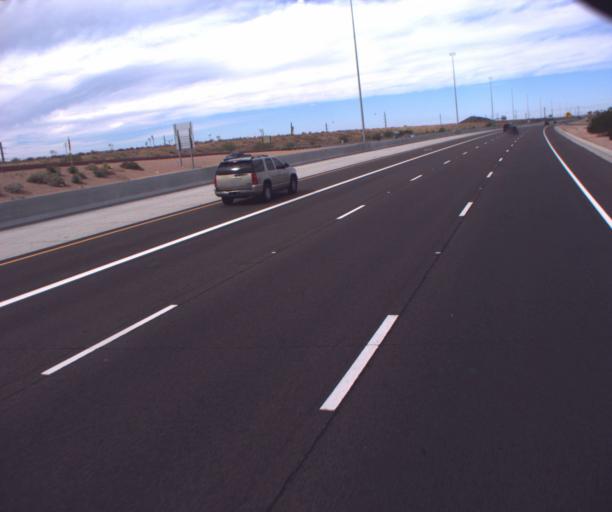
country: US
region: Arizona
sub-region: Pinal County
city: Apache Junction
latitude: 33.4384
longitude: -111.6531
